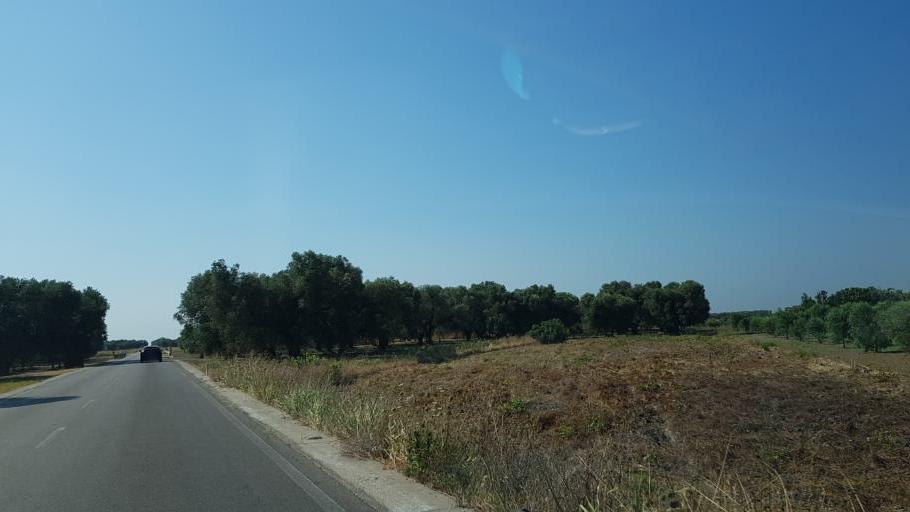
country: IT
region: Apulia
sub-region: Provincia di Brindisi
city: Mesagne
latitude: 40.5181
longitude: 17.8507
